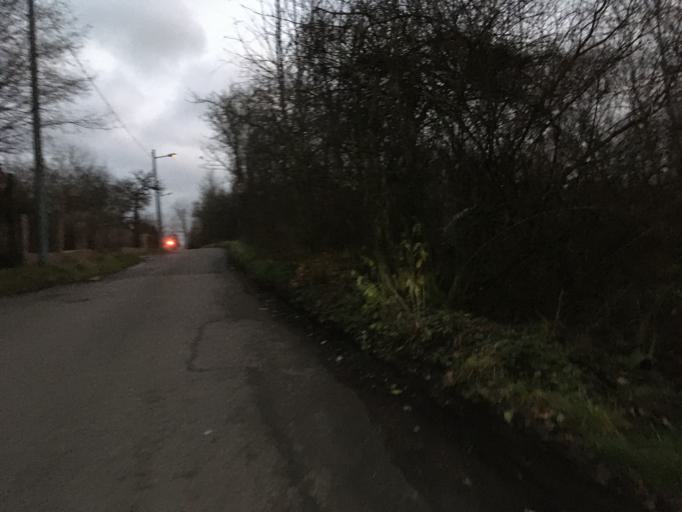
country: DE
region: Baden-Wuerttemberg
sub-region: Regierungsbezirk Stuttgart
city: Kornwestheim
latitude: 48.8374
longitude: 9.1984
